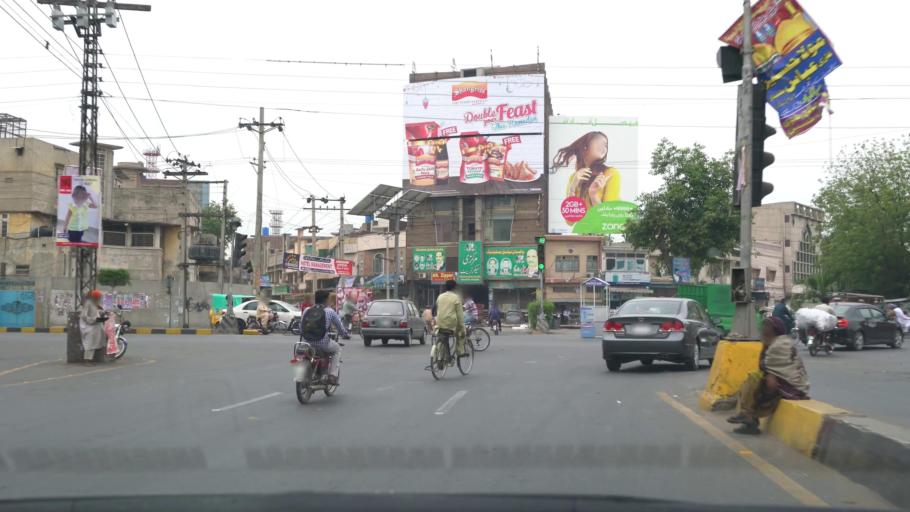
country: PK
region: Punjab
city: Faisalabad
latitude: 31.4228
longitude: 73.0693
